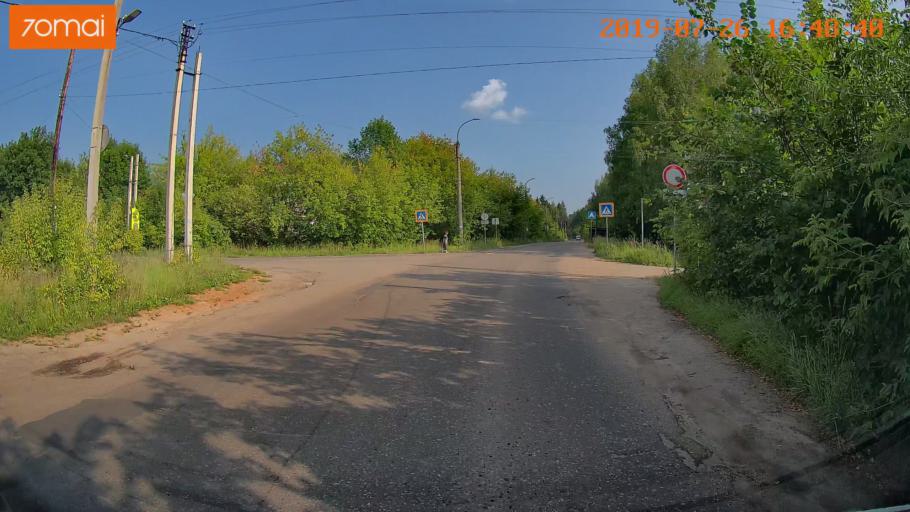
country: RU
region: Ivanovo
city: Bogorodskoye
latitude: 57.0332
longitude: 41.0167
